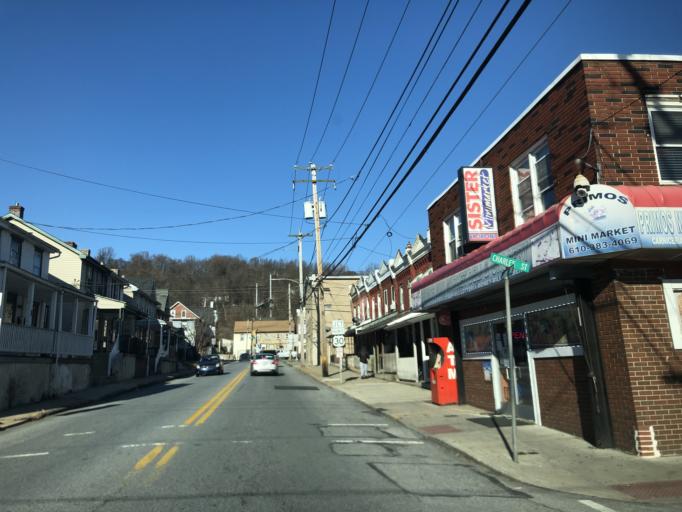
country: US
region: Pennsylvania
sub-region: Chester County
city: Coatesville
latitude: 39.9802
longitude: -75.8307
